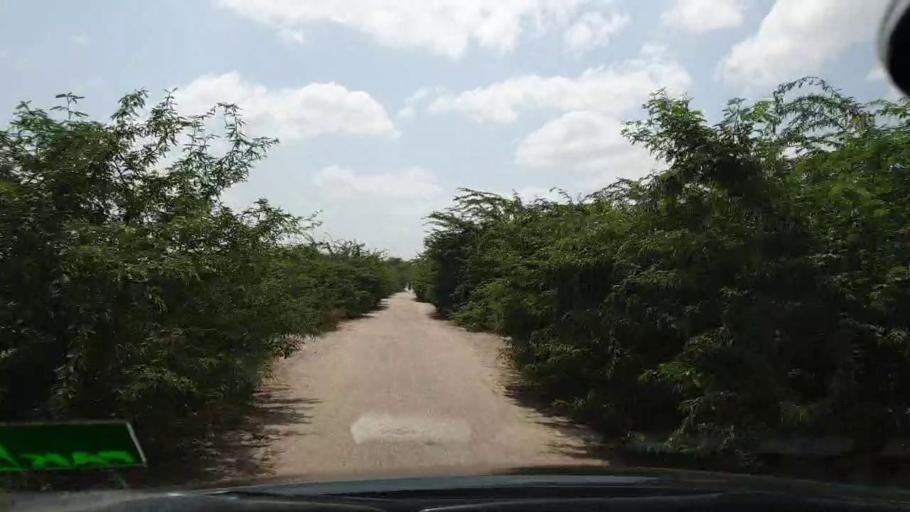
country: PK
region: Sindh
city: Kadhan
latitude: 24.5690
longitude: 69.2111
